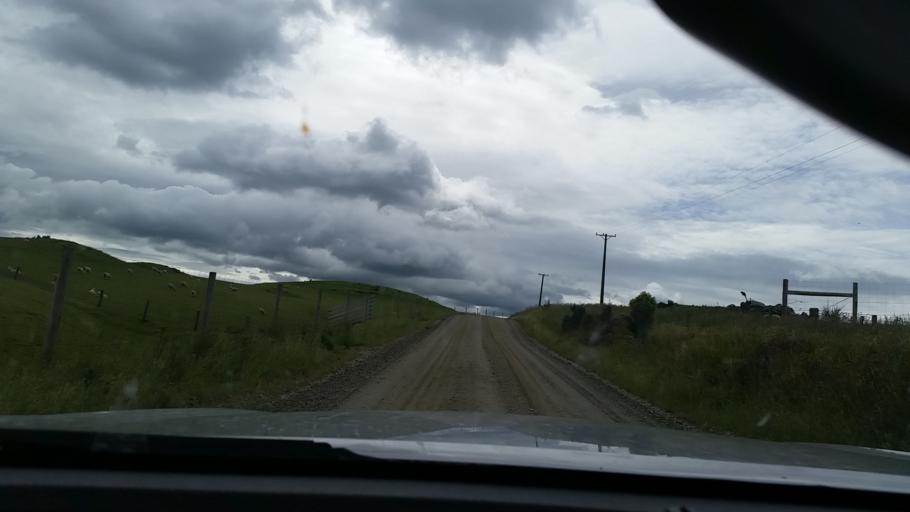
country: NZ
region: Southland
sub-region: Gore District
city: Gore
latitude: -46.2595
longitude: 168.9395
